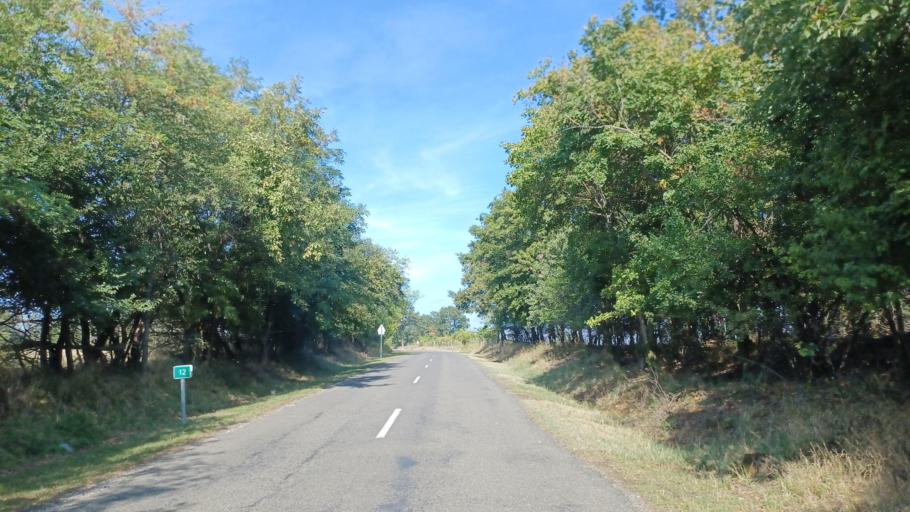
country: HU
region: Tolna
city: Pincehely
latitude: 46.6691
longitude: 18.4782
